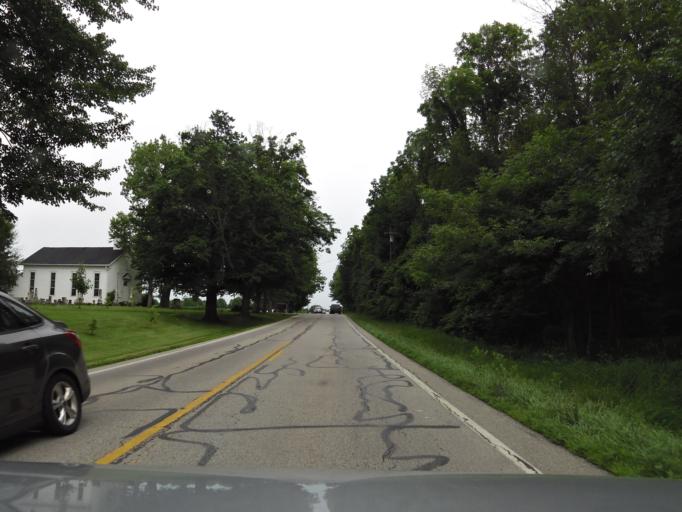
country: US
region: Ohio
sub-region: Warren County
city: Waynesville
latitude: 39.4964
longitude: -83.9812
